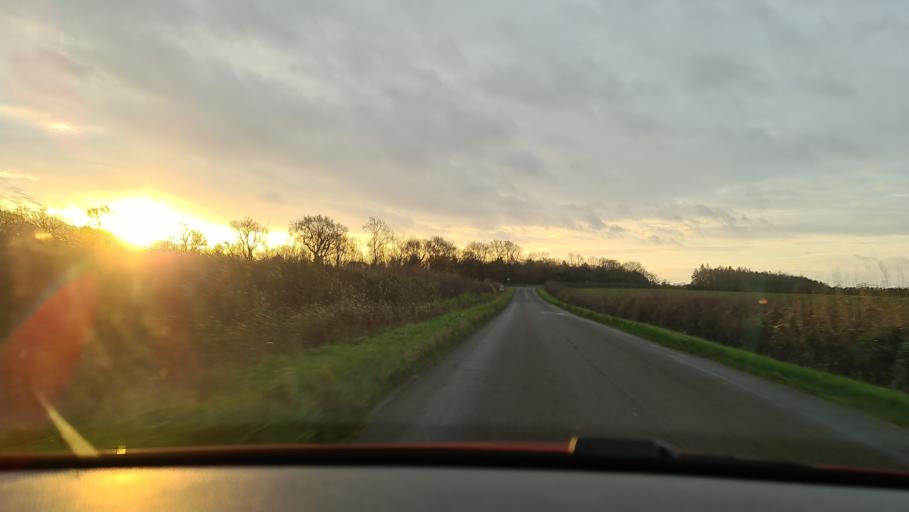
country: GB
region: England
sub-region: Oxfordshire
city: Somerton
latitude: 51.8930
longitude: -1.2741
